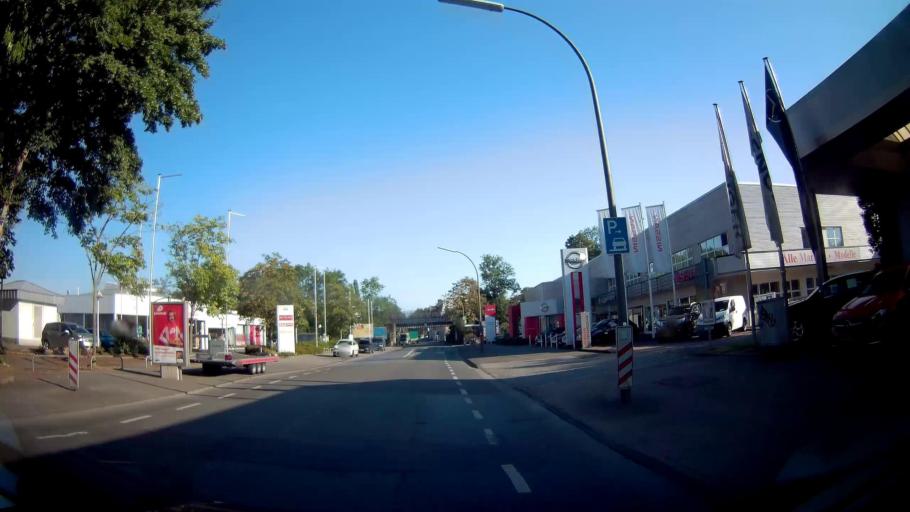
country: DE
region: North Rhine-Westphalia
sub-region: Regierungsbezirk Arnsberg
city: Dortmund
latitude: 51.5403
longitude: 7.4537
